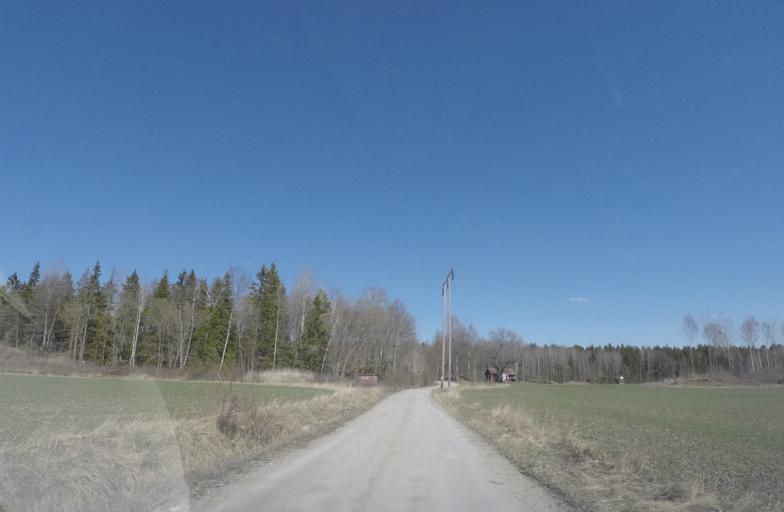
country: SE
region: Vaestmanland
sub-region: Vasteras
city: Vasteras
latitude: 59.6635
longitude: 16.4945
